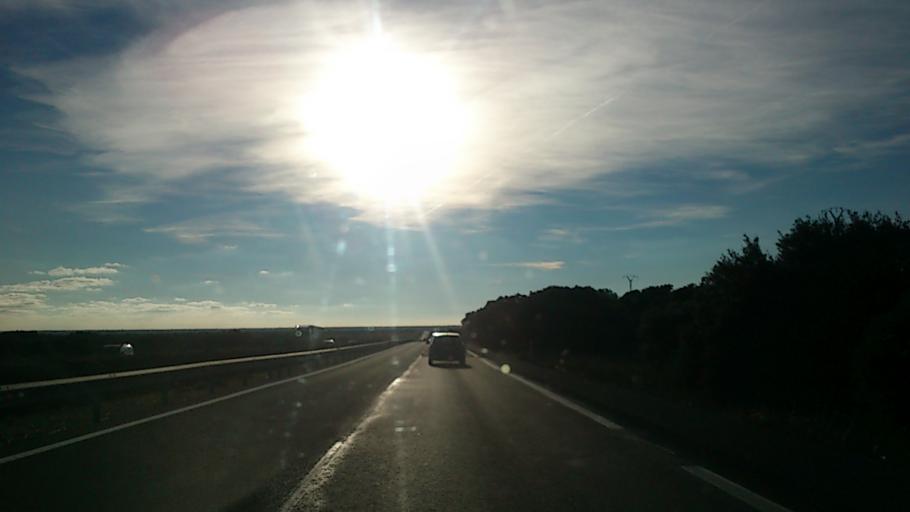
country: ES
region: Castille-La Mancha
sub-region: Provincia de Guadalajara
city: Algora
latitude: 40.9506
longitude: -2.6861
